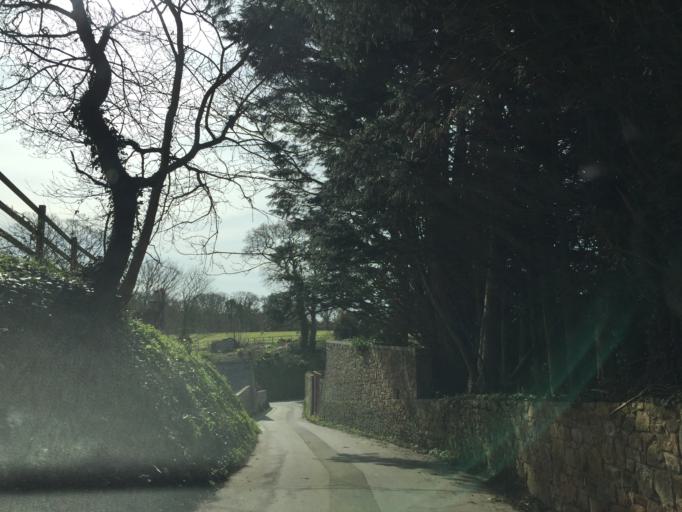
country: JE
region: St Helier
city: Saint Helier
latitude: 49.2205
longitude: -2.1482
